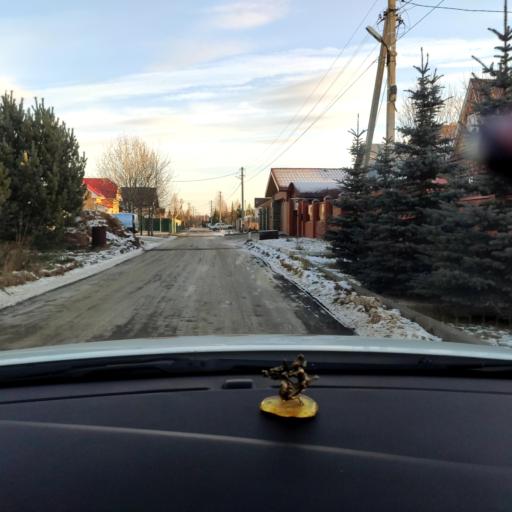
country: RU
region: Tatarstan
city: Stolbishchi
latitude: 55.6082
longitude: 49.1365
